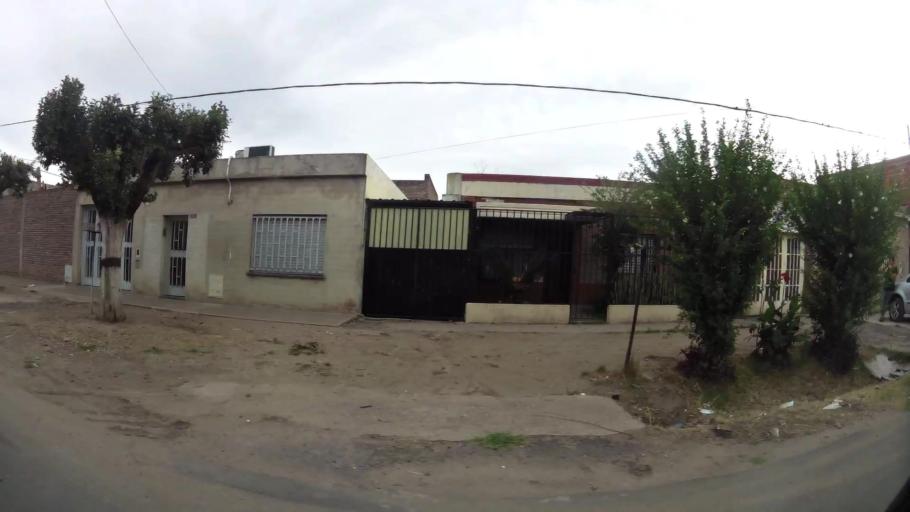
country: AR
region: Santa Fe
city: Gobernador Galvez
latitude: -33.0011
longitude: -60.6796
